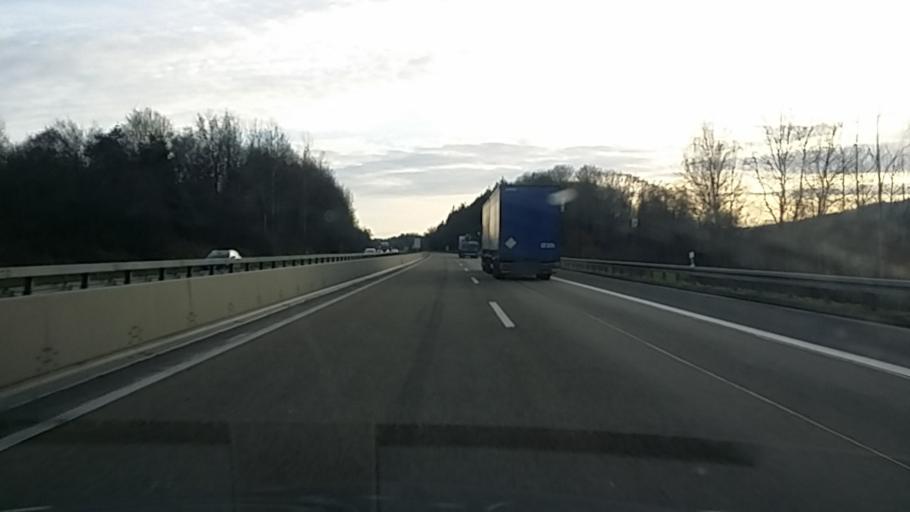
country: DE
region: Bavaria
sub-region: Regierungsbezirk Unterfranken
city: Motten
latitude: 50.4053
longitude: 9.7312
